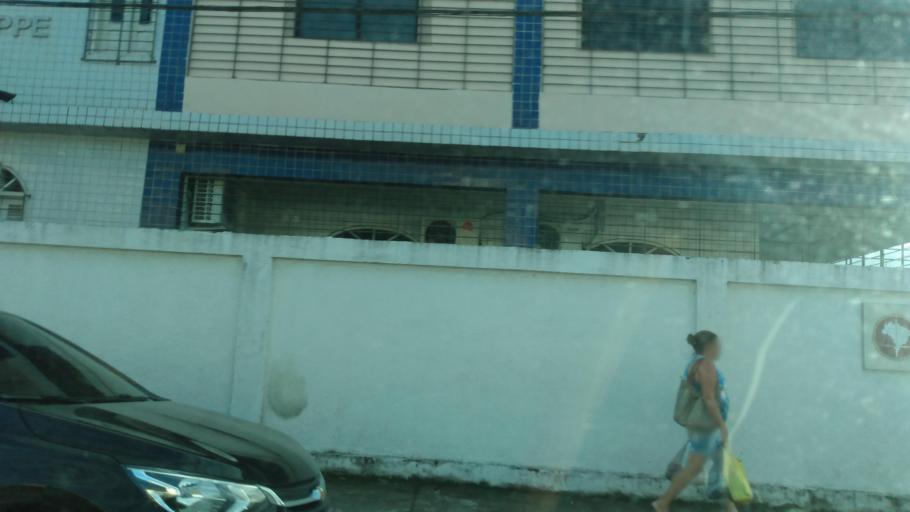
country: BR
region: Pernambuco
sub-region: Palmares
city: Palmares
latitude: -8.6834
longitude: -35.5971
